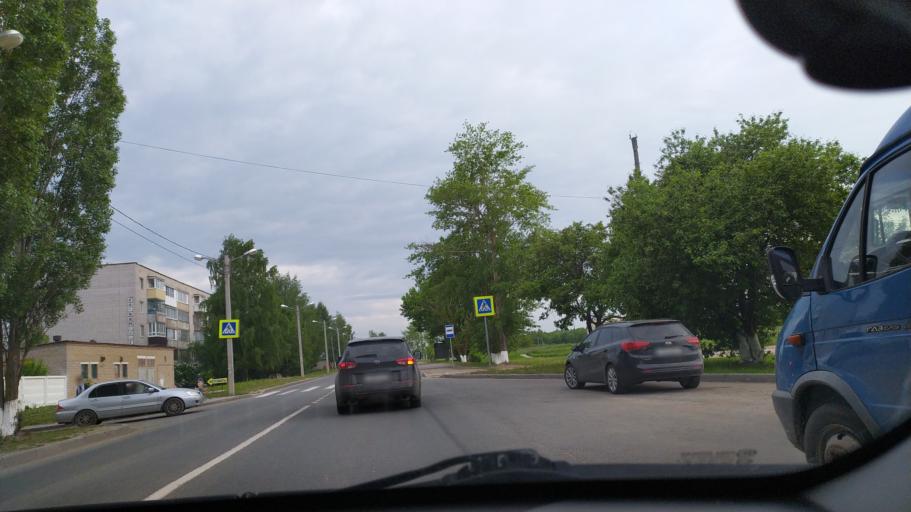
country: RU
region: Chuvashia
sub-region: Cheboksarskiy Rayon
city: Cheboksary
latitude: 56.1127
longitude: 47.2197
